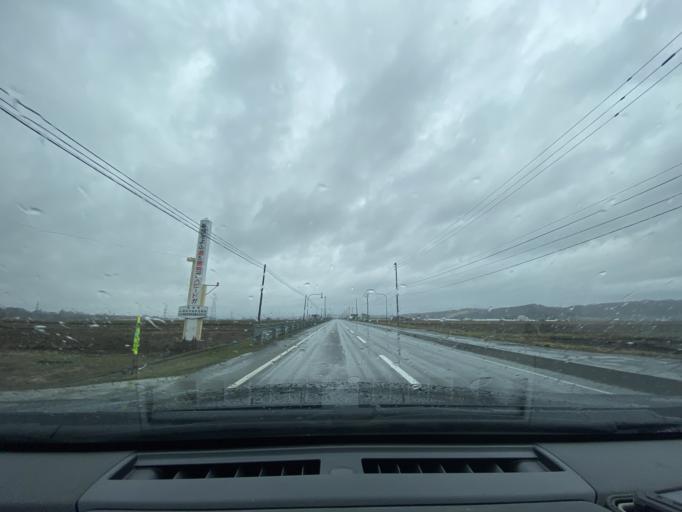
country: JP
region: Hokkaido
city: Fukagawa
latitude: 43.8165
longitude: 141.9925
